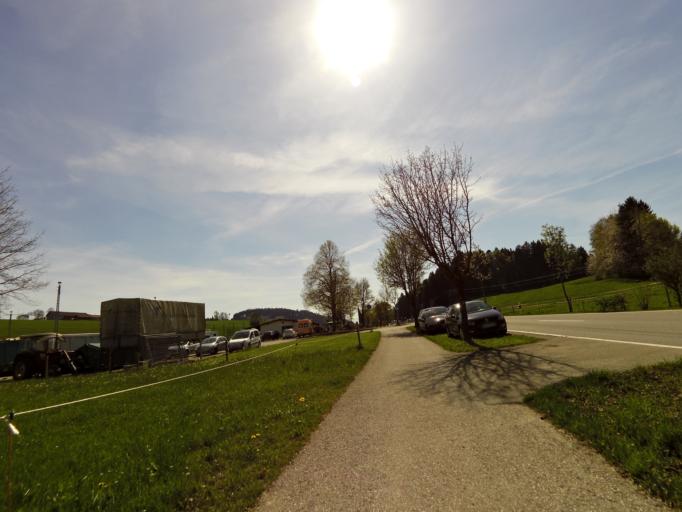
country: DE
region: Bavaria
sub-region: Swabia
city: Oberreute
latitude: 47.5944
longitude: 9.9518
